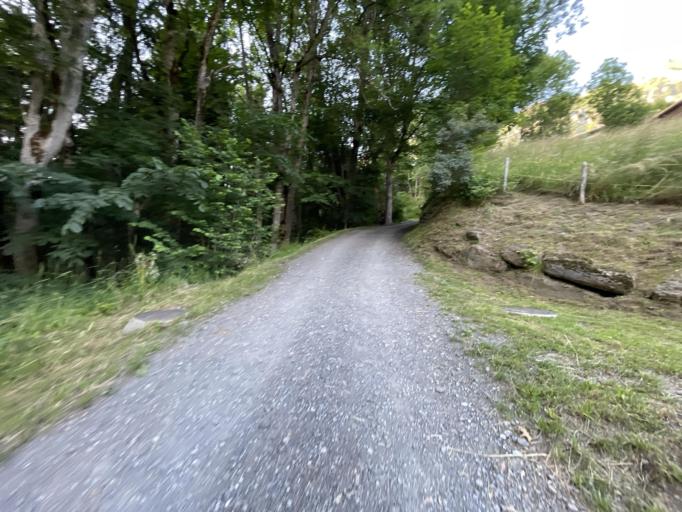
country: CH
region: Bern
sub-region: Interlaken-Oberhasli District
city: Lauterbrunnen
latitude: 46.6010
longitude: 7.9196
